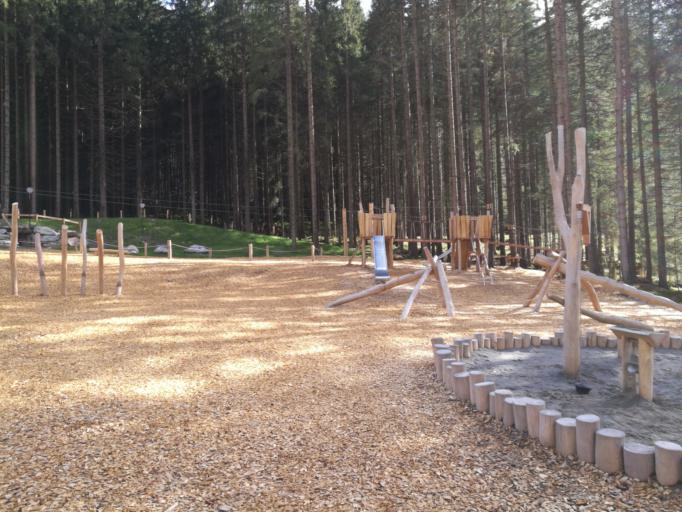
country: AT
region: Tyrol
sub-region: Politischer Bezirk Schwaz
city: Gerlos
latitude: 47.2185
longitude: 12.0207
